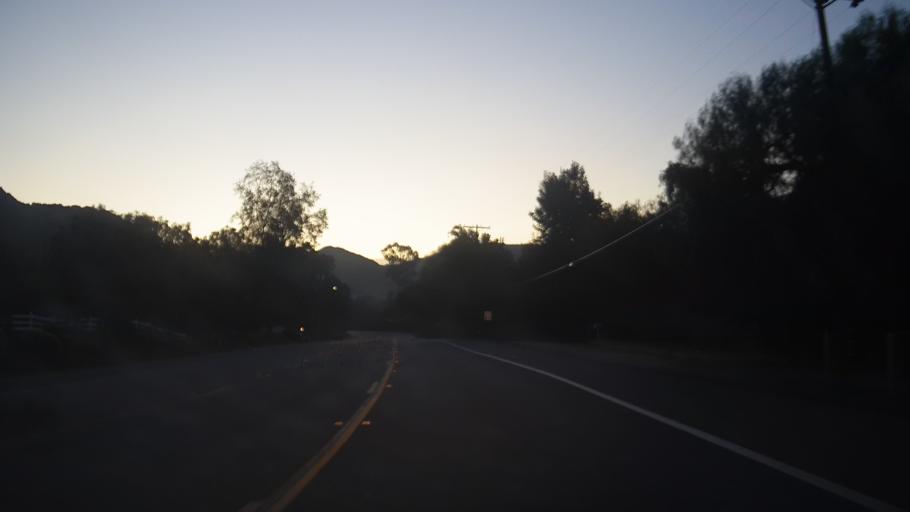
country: US
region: California
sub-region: San Diego County
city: Crest
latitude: 32.7819
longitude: -116.8754
